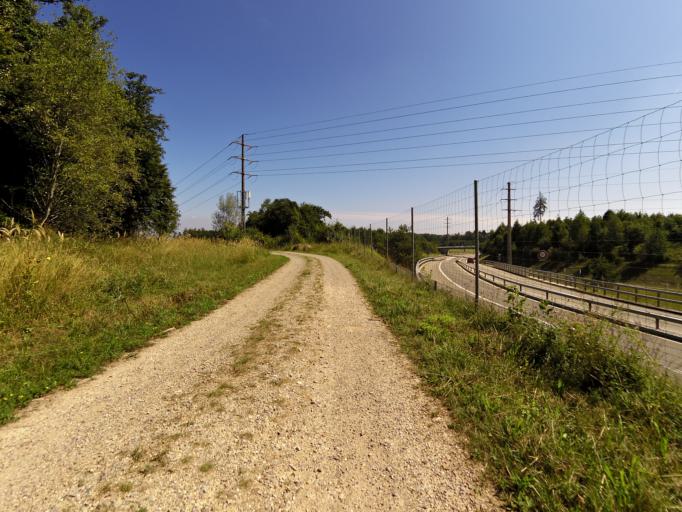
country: CH
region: Thurgau
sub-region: Kreuzlingen District
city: Tagerwilen
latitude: 47.6346
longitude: 9.1434
